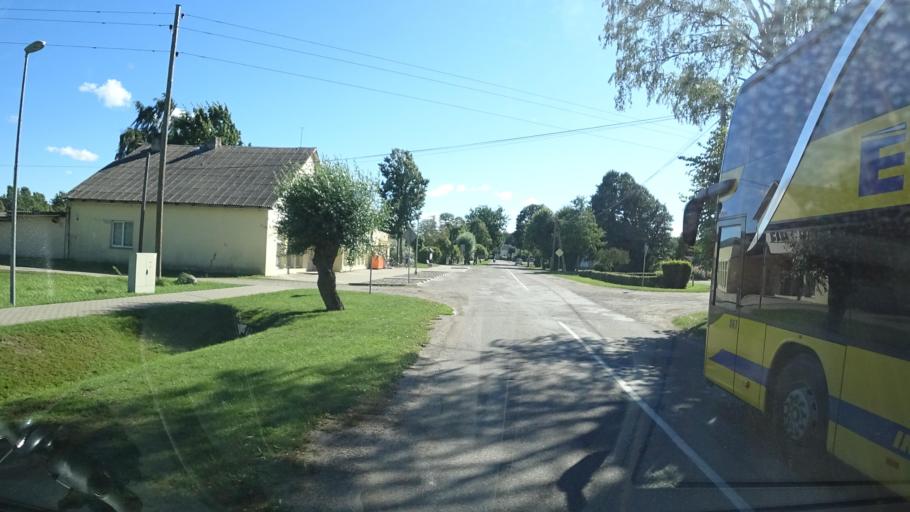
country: LV
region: Dundaga
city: Dundaga
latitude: 57.7441
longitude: 22.5868
